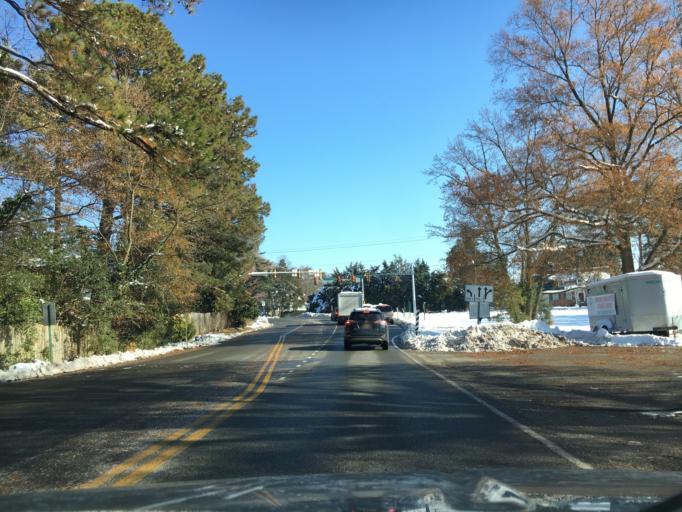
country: US
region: Virginia
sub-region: Henrico County
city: Tuckahoe
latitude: 37.5939
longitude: -77.5330
